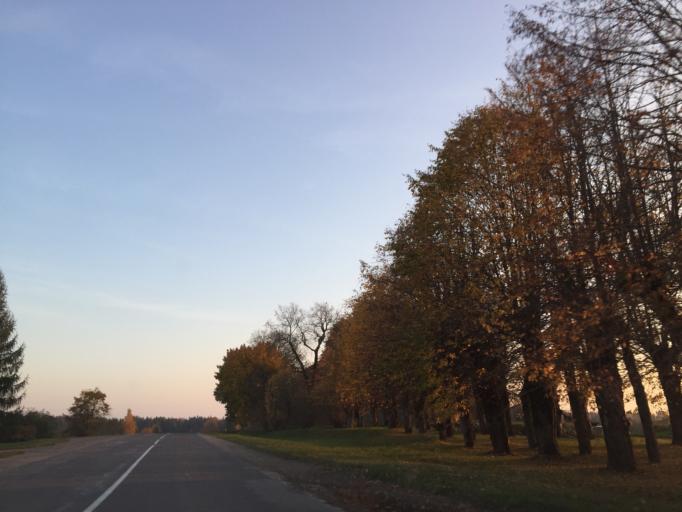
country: LV
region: Priekule
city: Priekule
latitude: 56.3667
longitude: 21.6029
